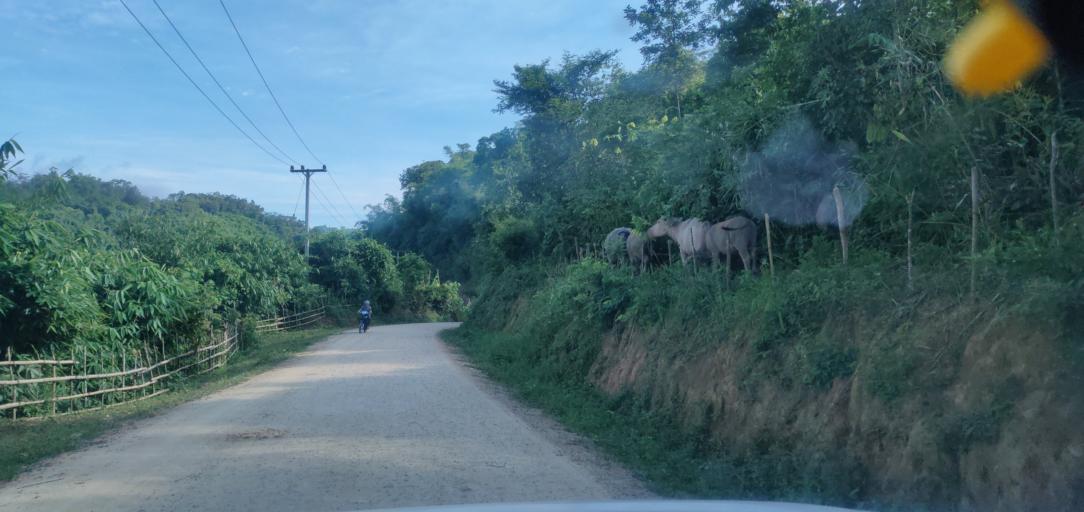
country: LA
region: Phongsali
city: Khoa
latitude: 21.2040
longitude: 102.6841
